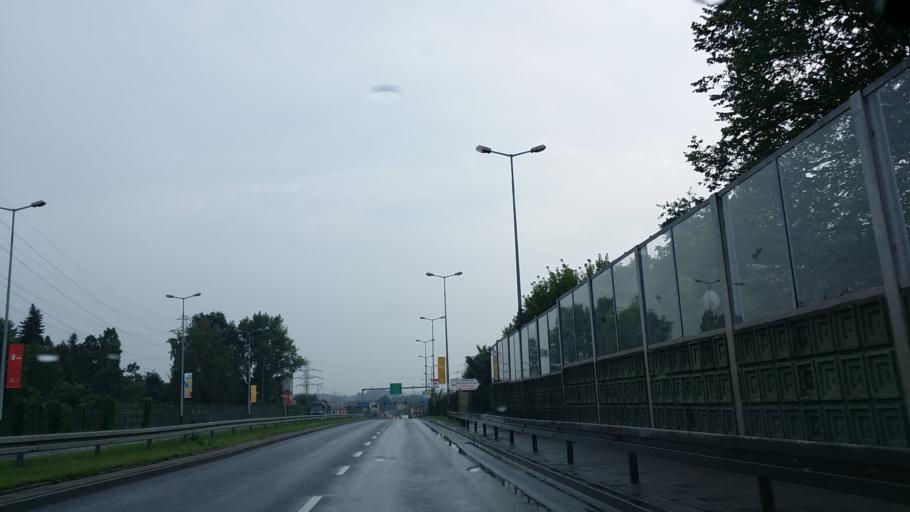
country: PL
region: Lesser Poland Voivodeship
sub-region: Krakow
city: Krakow
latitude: 50.0175
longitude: 19.9454
